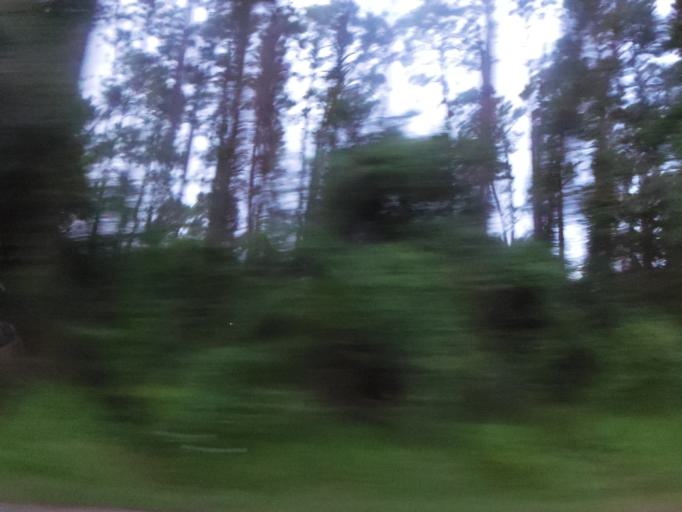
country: US
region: Florida
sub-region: Duval County
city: Jacksonville
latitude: 30.2419
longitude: -81.6102
